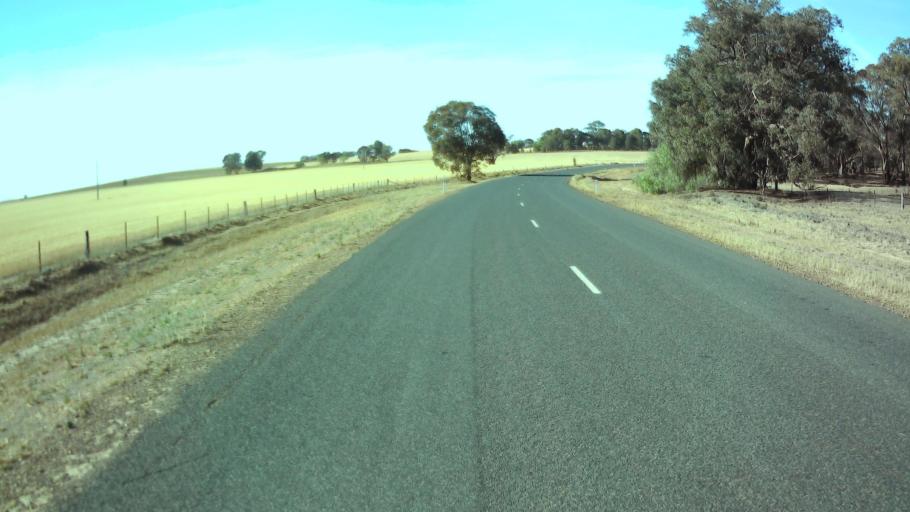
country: AU
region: New South Wales
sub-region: Weddin
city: Grenfell
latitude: -33.9853
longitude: 148.1408
